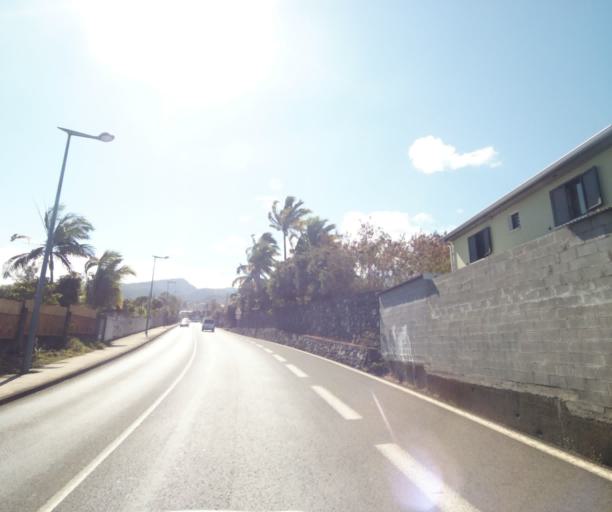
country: RE
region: Reunion
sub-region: Reunion
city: Le Port
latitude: -20.9781
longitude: 55.3217
